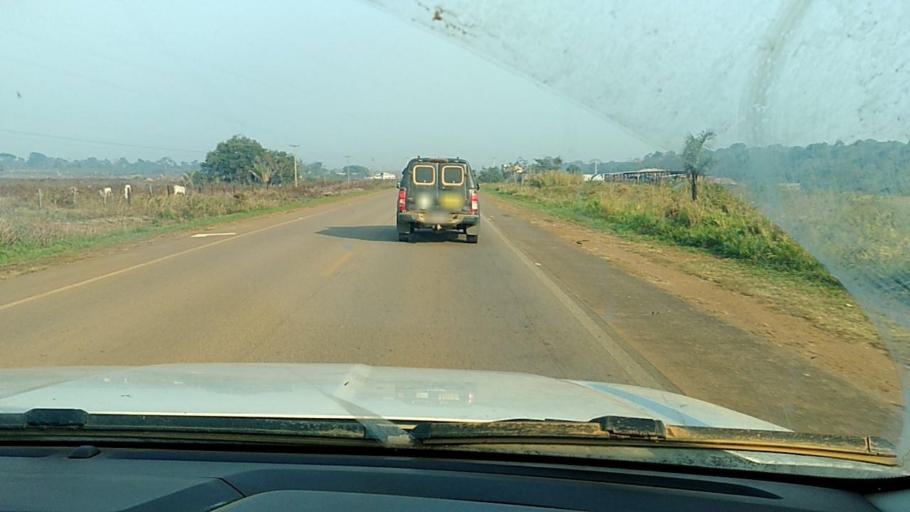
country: BR
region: Rondonia
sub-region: Porto Velho
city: Porto Velho
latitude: -8.7390
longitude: -63.9568
